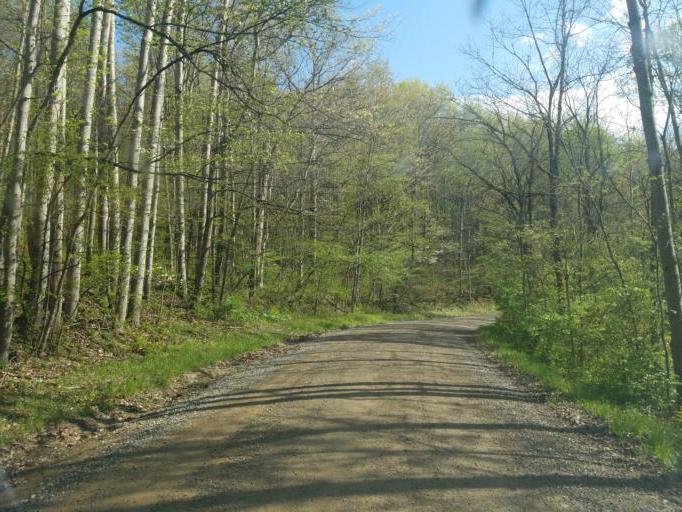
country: US
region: Ohio
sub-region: Knox County
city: Oak Hill
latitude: 40.3948
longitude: -82.2276
